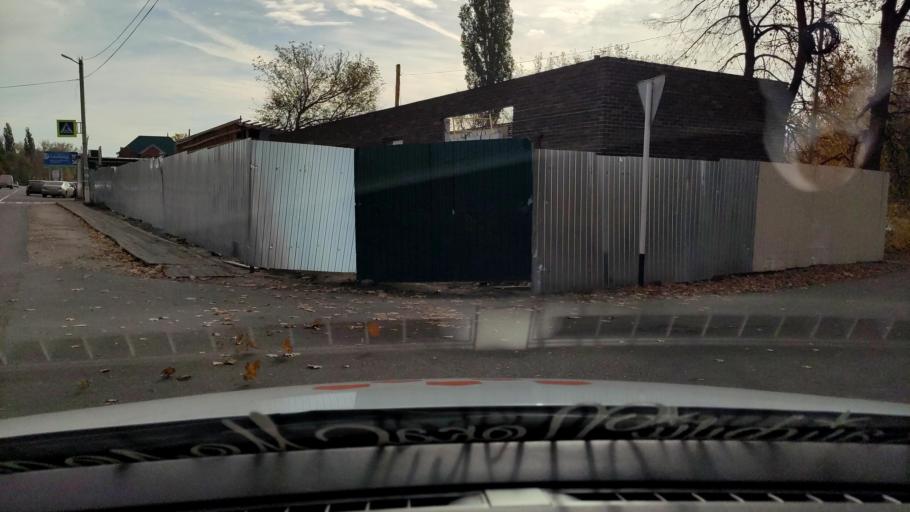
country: RU
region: Voronezj
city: Ramon'
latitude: 51.9103
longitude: 39.3309
